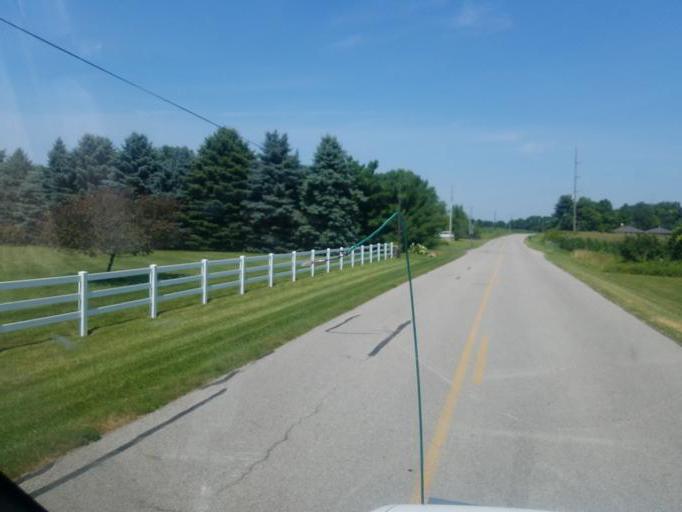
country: US
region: Ohio
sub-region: Logan County
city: West Liberty
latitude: 40.2668
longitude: -83.7636
